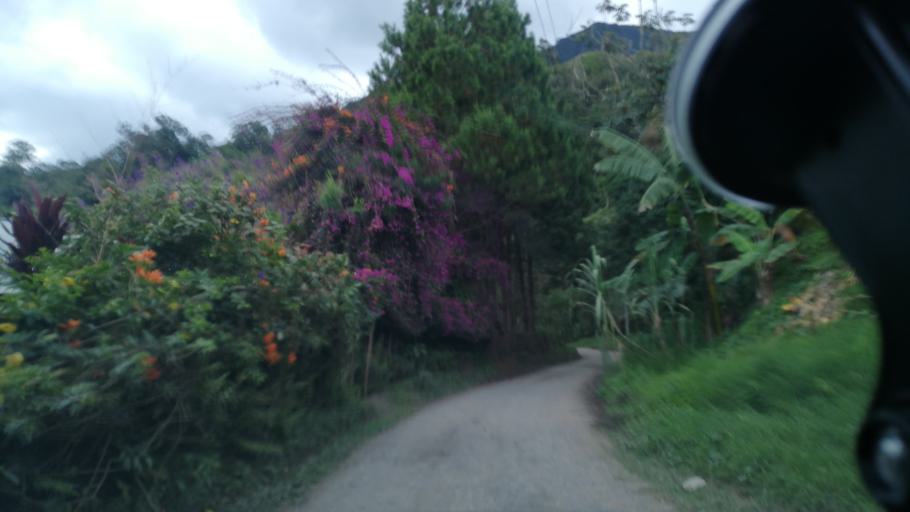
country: CO
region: Cundinamarca
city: Pacho
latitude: 5.1577
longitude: -74.2404
